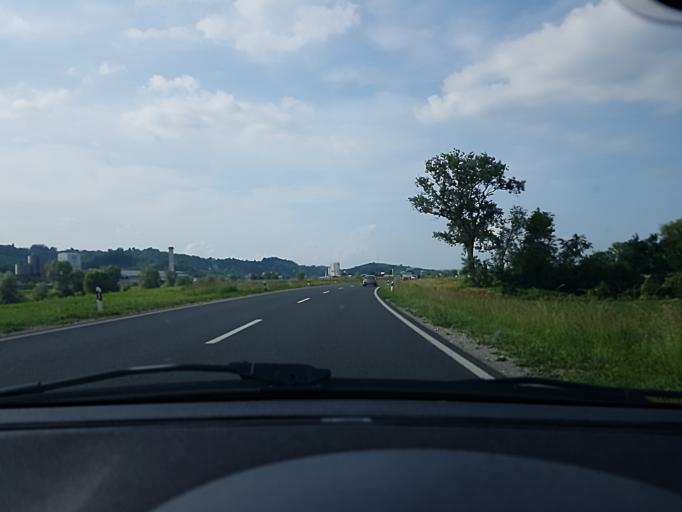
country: HR
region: Zagrebacka
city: Pojatno
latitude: 45.9045
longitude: 15.8125
